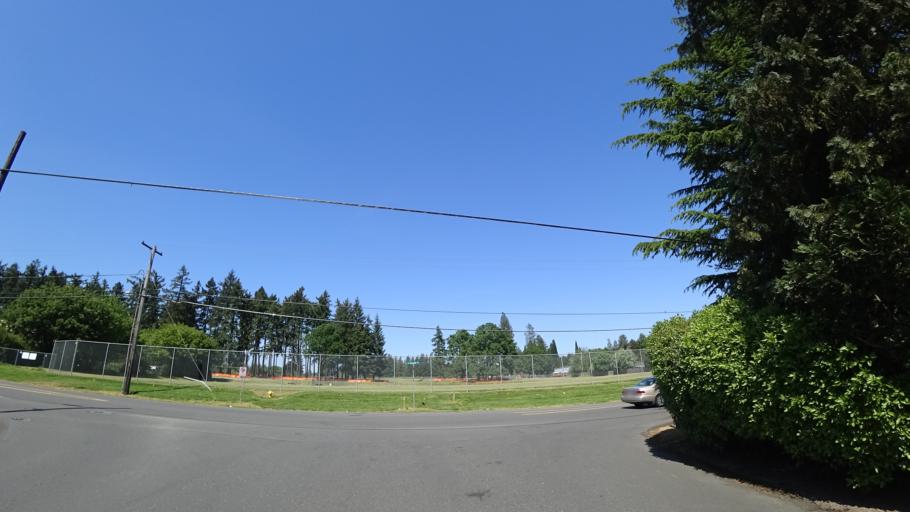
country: US
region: Oregon
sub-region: Washington County
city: Cedar Hills
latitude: 45.5004
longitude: -122.8034
